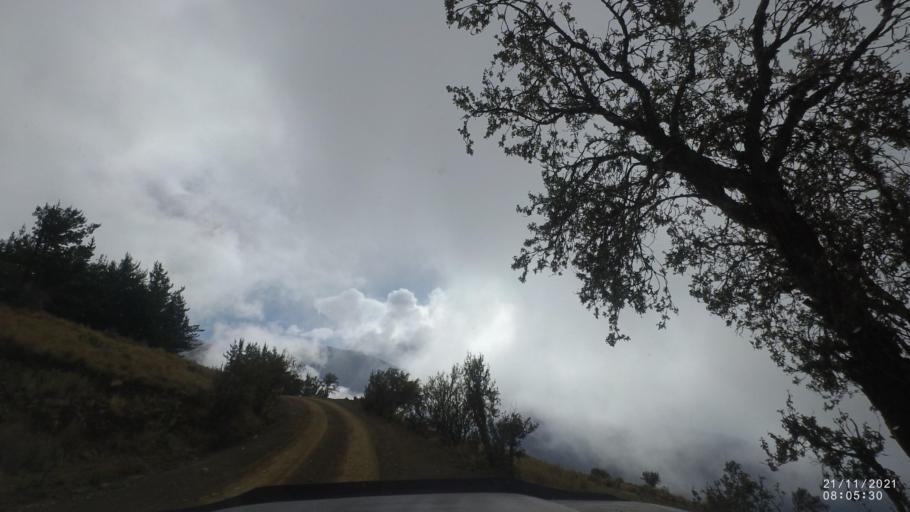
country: BO
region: Cochabamba
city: Cochabamba
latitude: -17.2890
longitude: -66.2105
